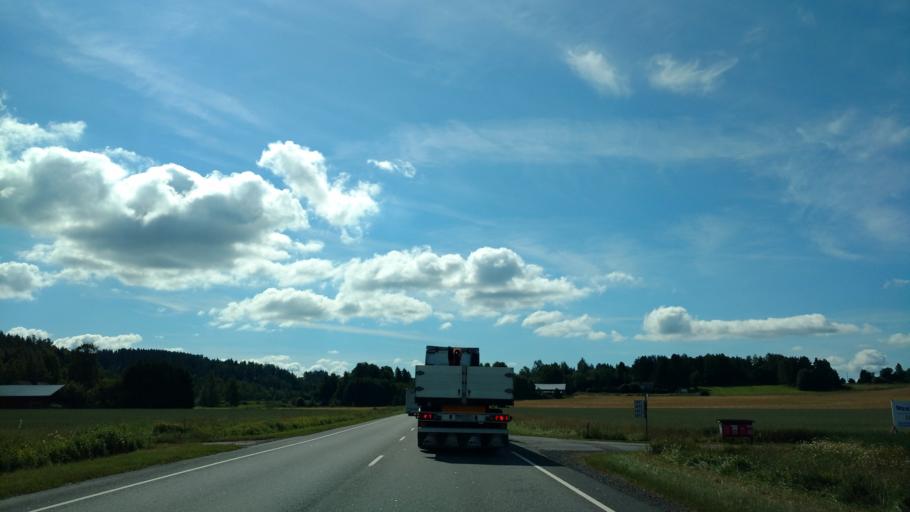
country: FI
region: Varsinais-Suomi
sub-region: Salo
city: Pernioe
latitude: 60.2615
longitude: 23.1306
